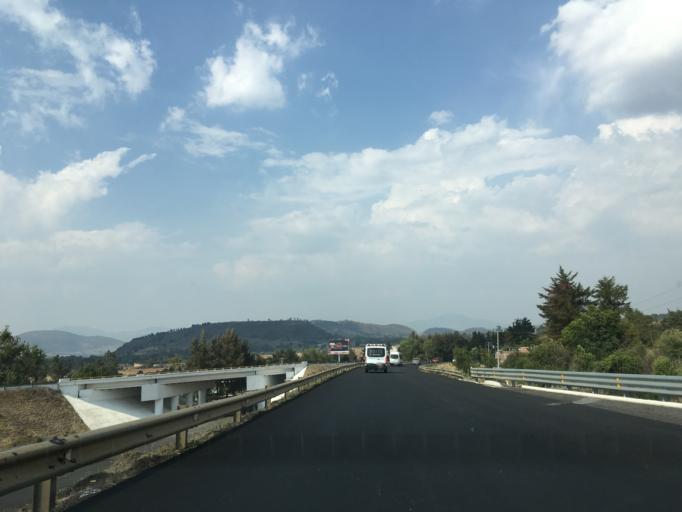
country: MX
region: Michoacan
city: Patzcuaro
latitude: 19.5294
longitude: -101.5624
